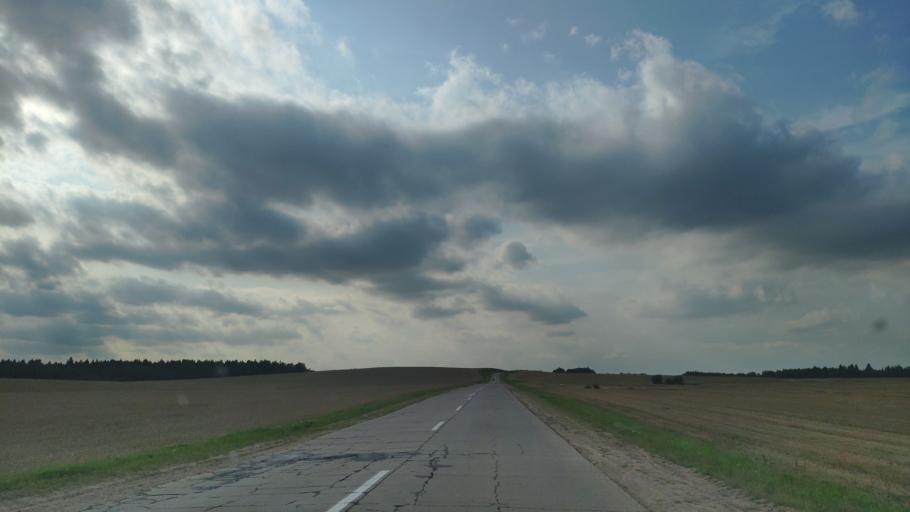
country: BY
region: Minsk
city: Khatsyezhyna
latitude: 53.8341
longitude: 27.3021
